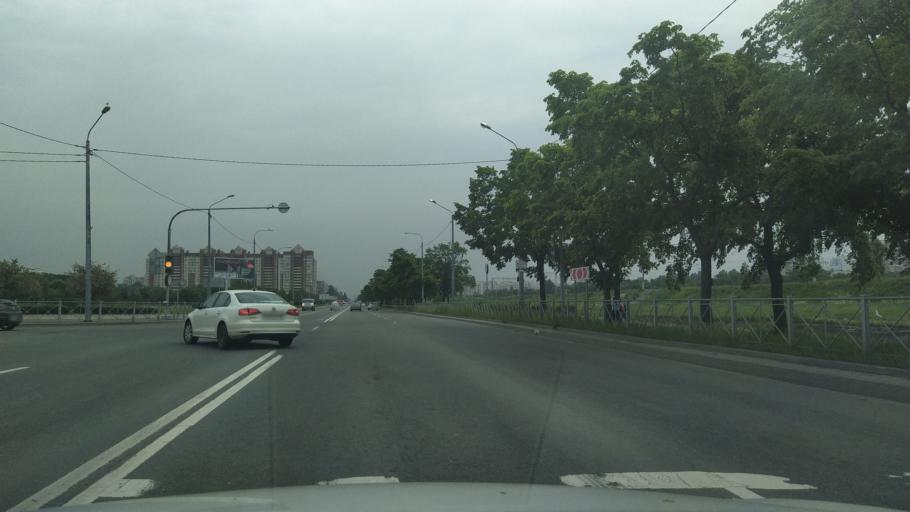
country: RU
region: St.-Petersburg
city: Kupchino
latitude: 59.8664
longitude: 30.3597
